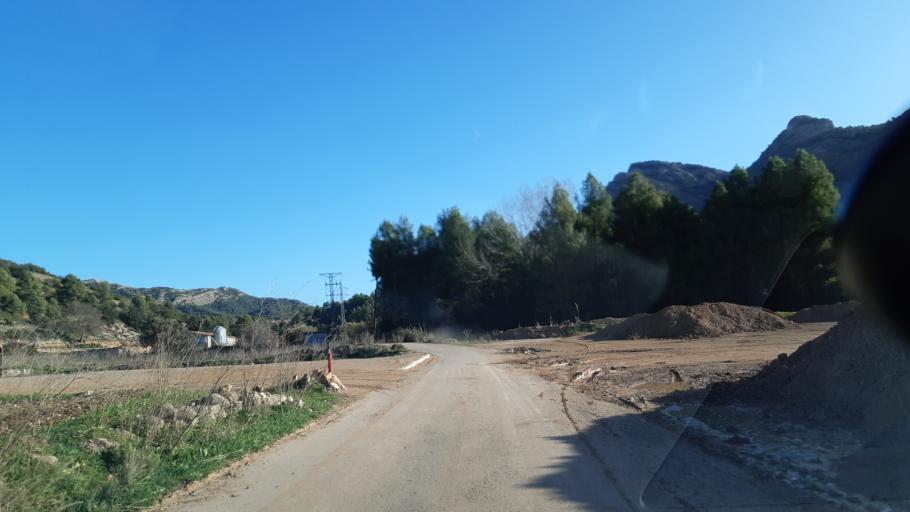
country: ES
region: Aragon
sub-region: Provincia de Teruel
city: Valderrobres
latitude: 40.8428
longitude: 0.2025
